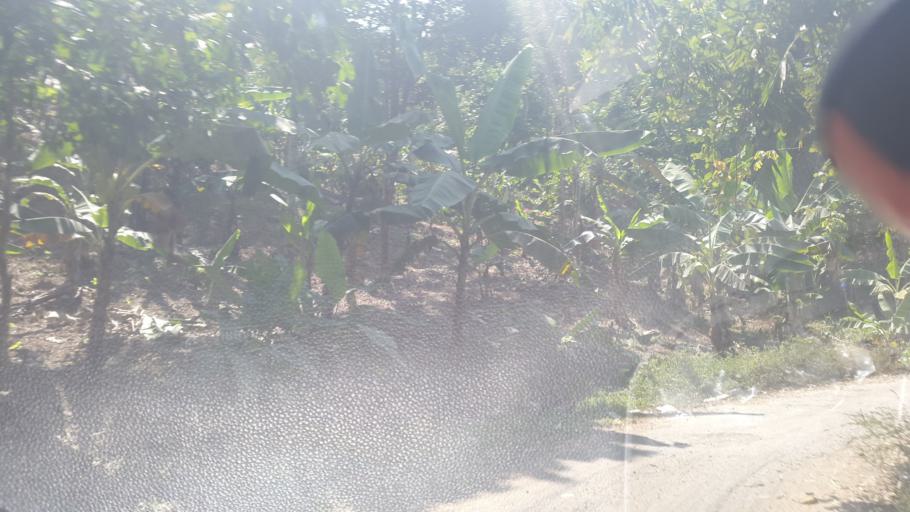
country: ID
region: West Java
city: Gunungkalong
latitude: -6.9332
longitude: 106.7875
